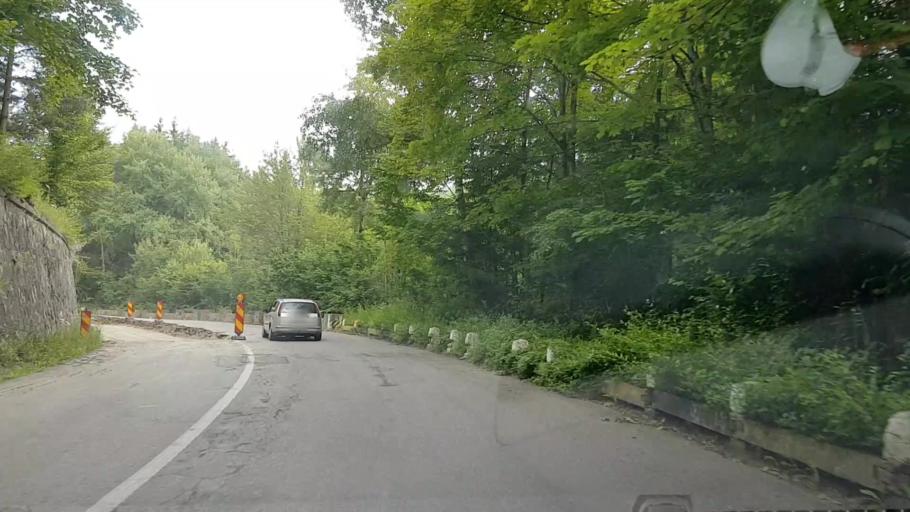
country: RO
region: Neamt
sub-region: Comuna Pangarati
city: Pangarati
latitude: 46.9421
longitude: 26.1245
